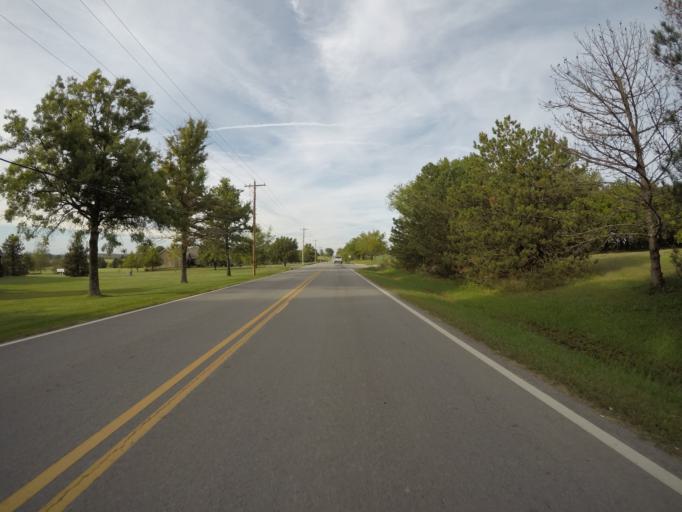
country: US
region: Kansas
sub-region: Douglas County
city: Baldwin City
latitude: 38.7764
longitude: -95.2050
